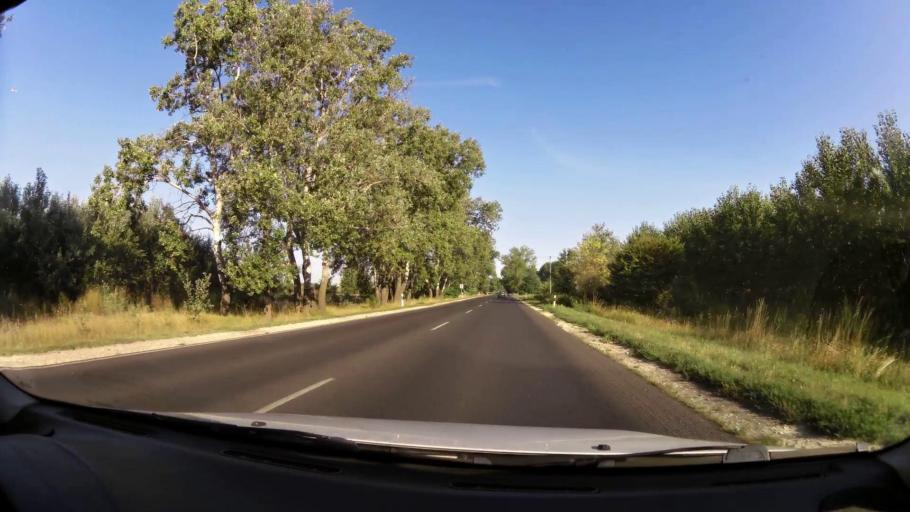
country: HU
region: Pest
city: Monor
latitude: 47.3238
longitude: 19.4651
